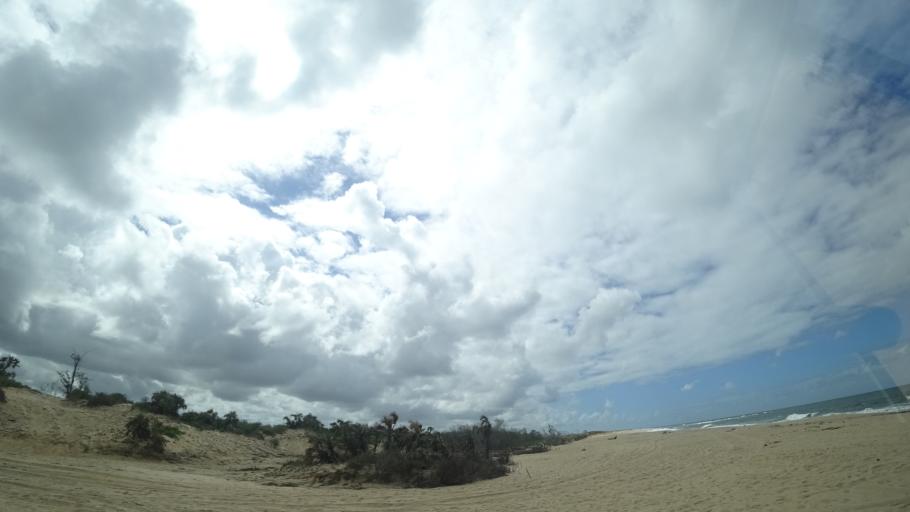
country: MZ
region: Sofala
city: Beira
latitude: -19.6120
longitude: 35.2247
